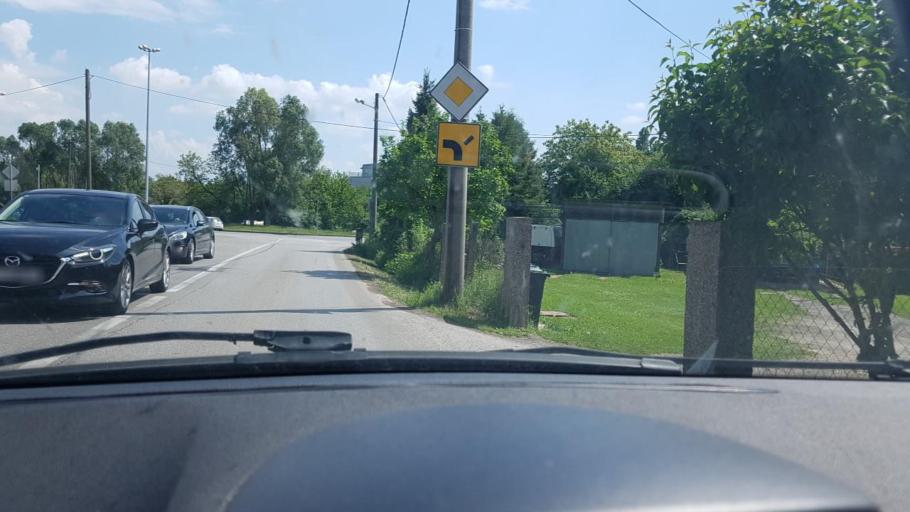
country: HR
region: Grad Zagreb
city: Dubrava
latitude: 45.8411
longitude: 16.0286
